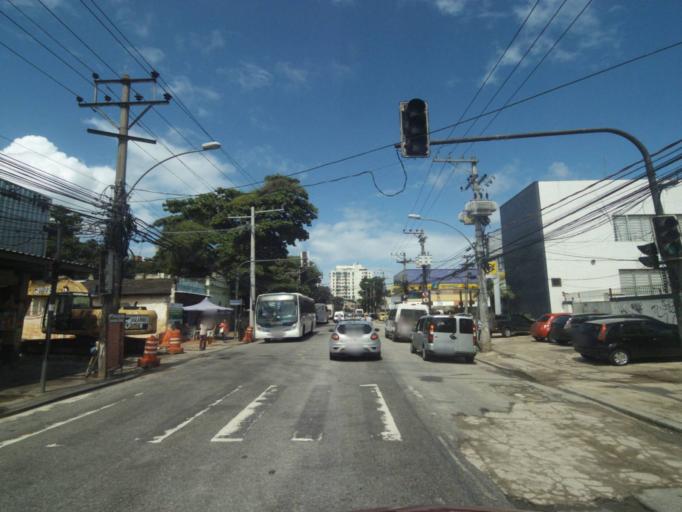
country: BR
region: Rio de Janeiro
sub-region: Sao Joao De Meriti
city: Sao Joao de Meriti
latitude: -22.9178
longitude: -43.3611
